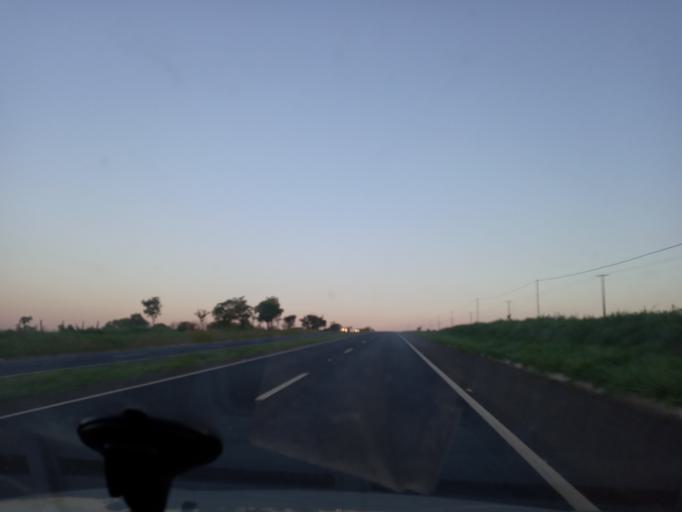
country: BR
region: Minas Gerais
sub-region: Uberlandia
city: Uberlandia
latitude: -18.8847
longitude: -48.4703
